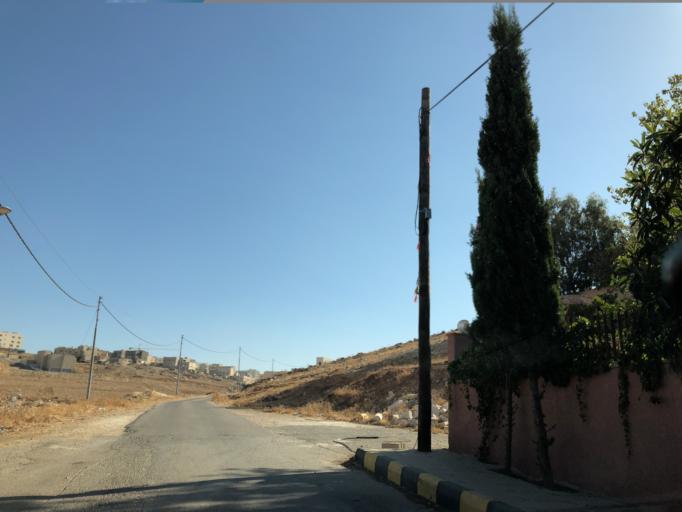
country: JO
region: Amman
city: Wadi as Sir
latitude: 31.9329
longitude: 35.8398
